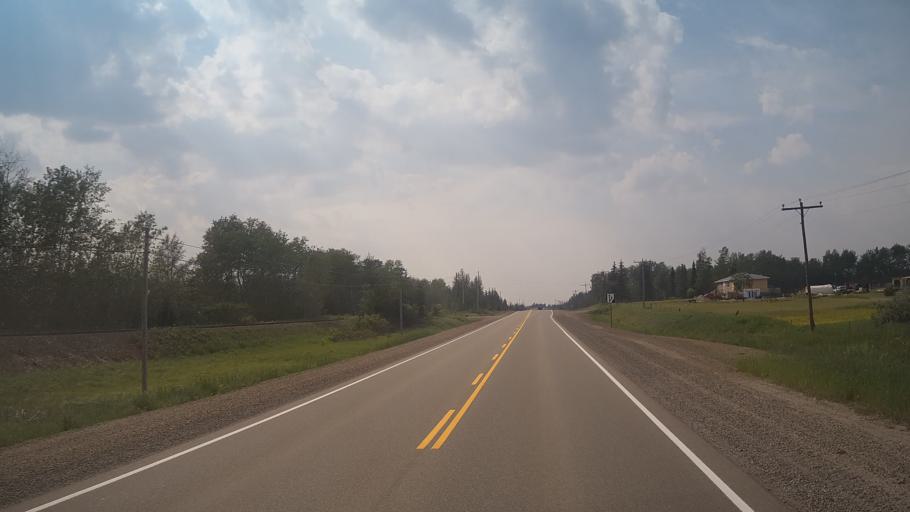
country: CA
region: Ontario
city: Kapuskasing
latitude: 49.4541
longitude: -82.5653
